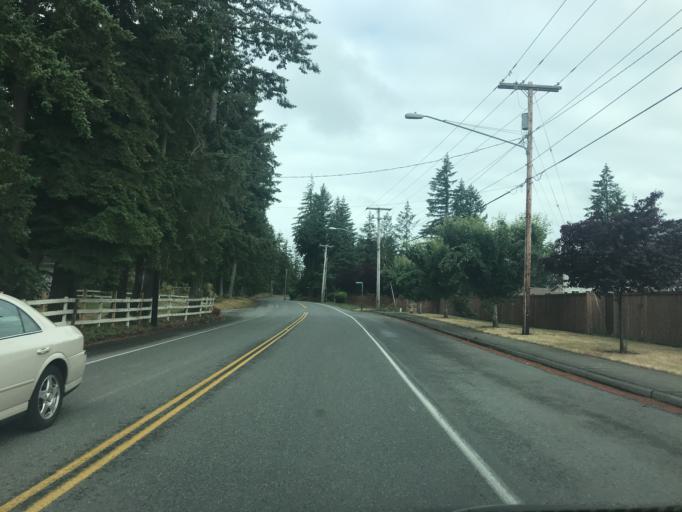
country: US
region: Washington
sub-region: King County
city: Lake Morton-Berrydale
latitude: 47.3418
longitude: -122.0586
